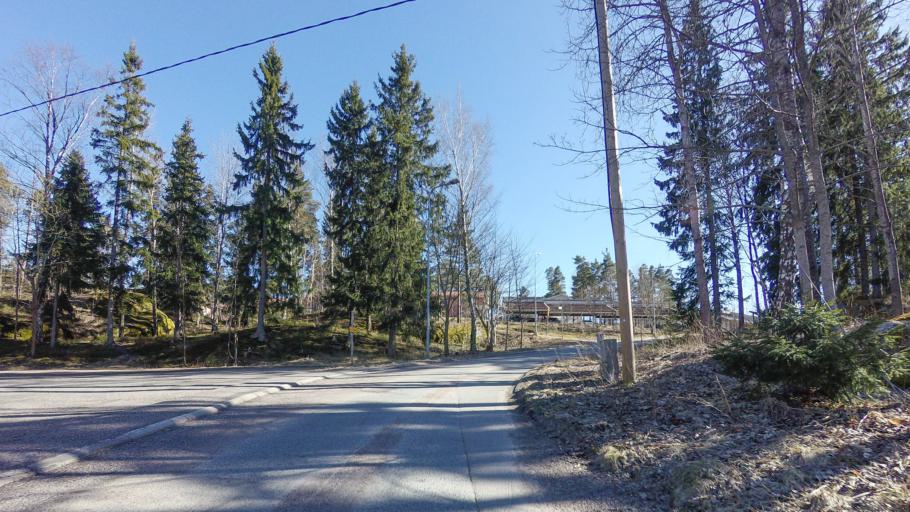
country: FI
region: Uusimaa
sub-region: Helsinki
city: Vantaa
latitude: 60.1693
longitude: 25.0835
